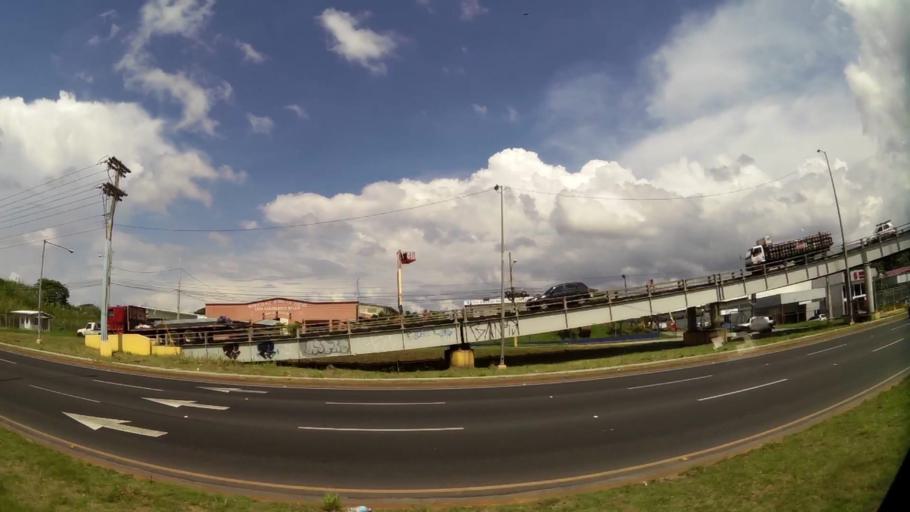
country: PA
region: Panama
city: San Miguelito
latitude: 9.0497
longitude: -79.4572
